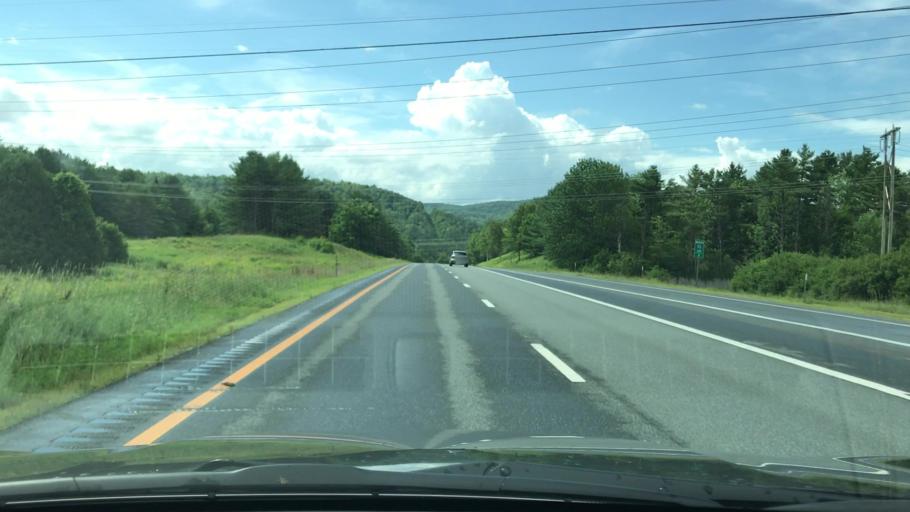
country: US
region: New Hampshire
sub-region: Grafton County
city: Littleton
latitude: 44.3323
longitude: -71.8801
